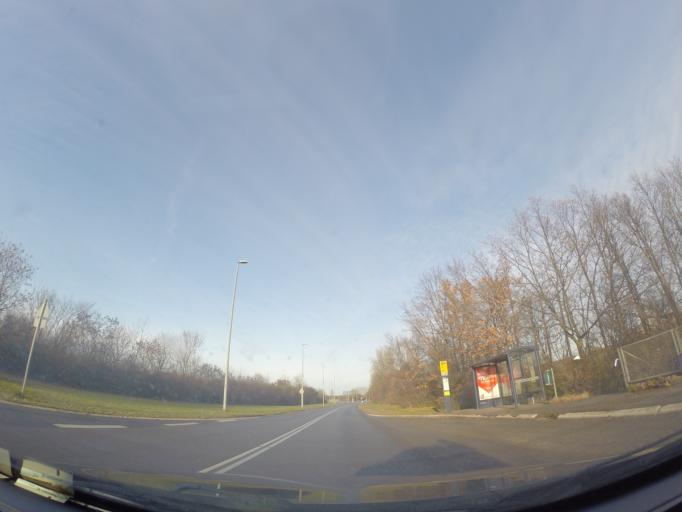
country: DK
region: Capital Region
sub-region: Hoje-Taastrup Kommune
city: Taastrup
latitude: 55.6524
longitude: 12.2665
